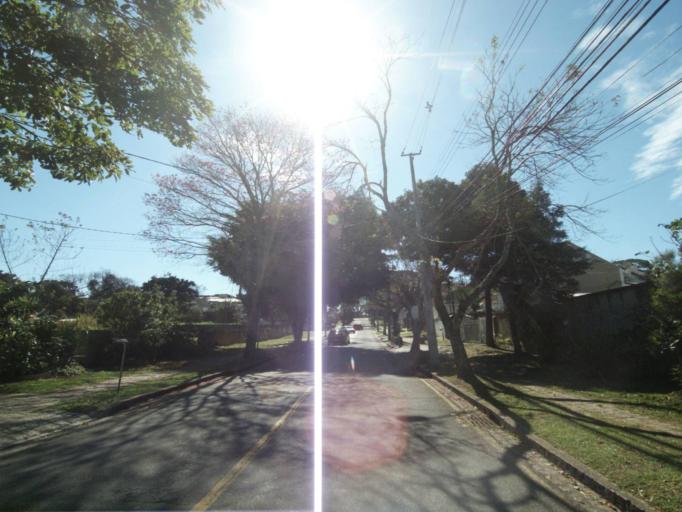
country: BR
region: Parana
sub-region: Curitiba
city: Curitiba
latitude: -25.4131
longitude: -49.2757
